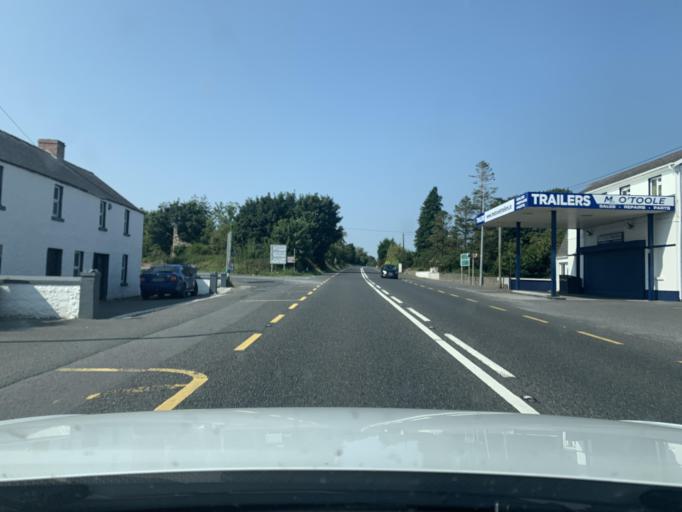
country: IE
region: Leinster
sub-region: An Iarmhi
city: Athlone
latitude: 53.4705
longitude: -8.0169
